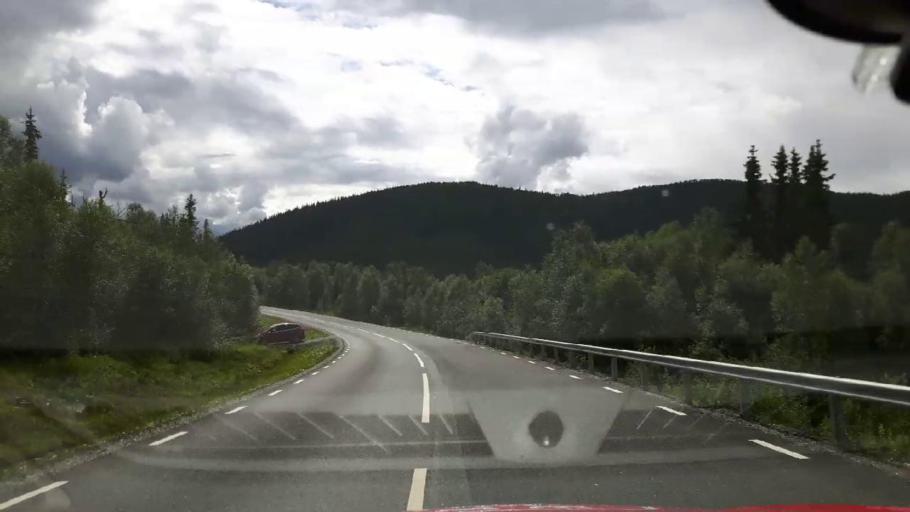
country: NO
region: Nord-Trondelag
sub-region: Royrvik
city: Royrvik
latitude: 64.8895
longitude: 14.1903
